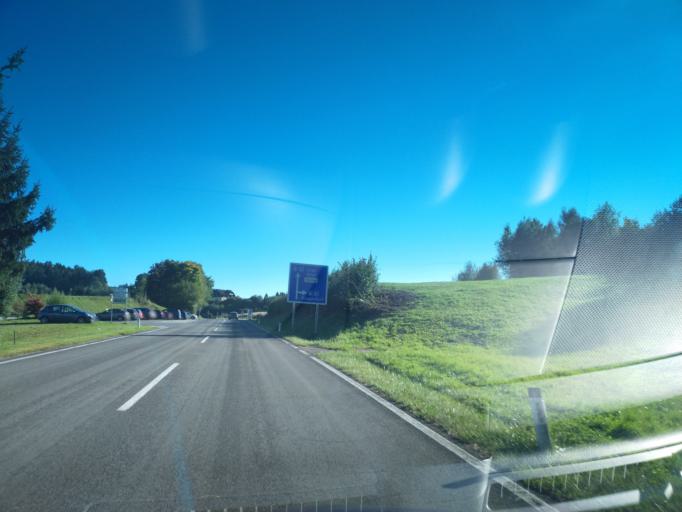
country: AT
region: Styria
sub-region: Politischer Bezirk Deutschlandsberg
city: Gundersdorf
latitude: 46.9650
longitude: 15.2191
